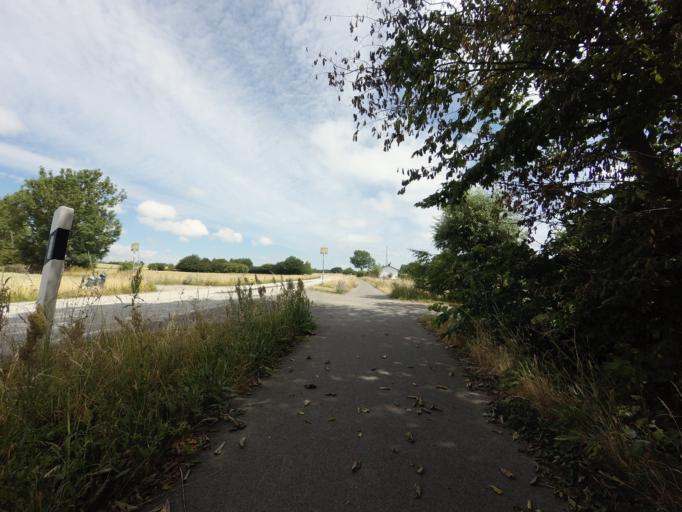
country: SE
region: Skane
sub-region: Simrishamns Kommun
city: Simrishamn
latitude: 55.5084
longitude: 14.3347
